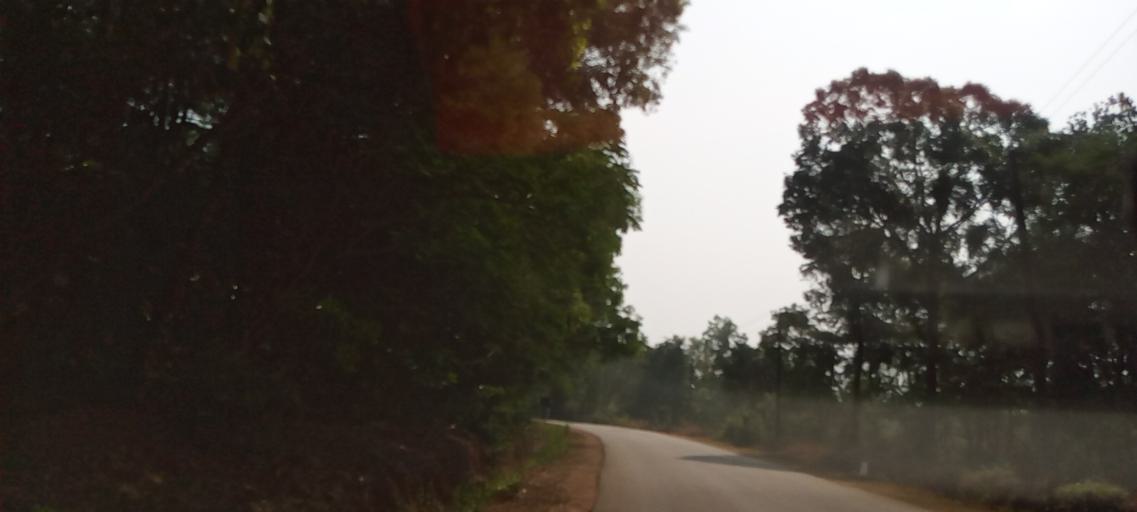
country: IN
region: Karnataka
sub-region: Udupi
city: Someshwar
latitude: 13.5171
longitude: 74.9367
